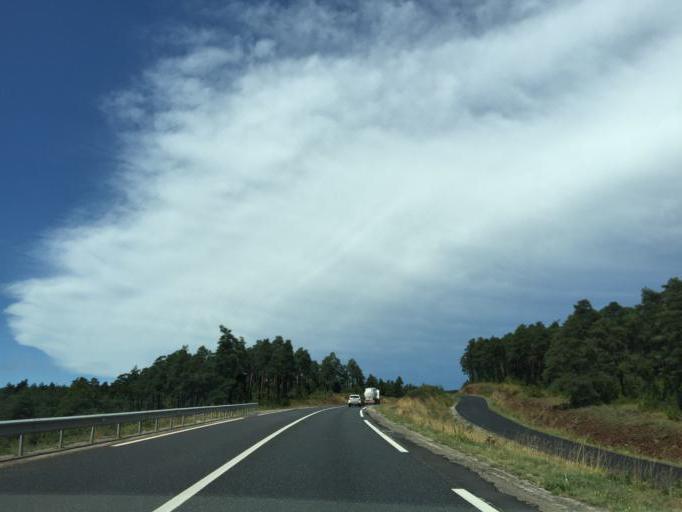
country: FR
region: Midi-Pyrenees
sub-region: Departement de l'Aveyron
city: Millau
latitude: 44.1828
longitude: 3.0283
